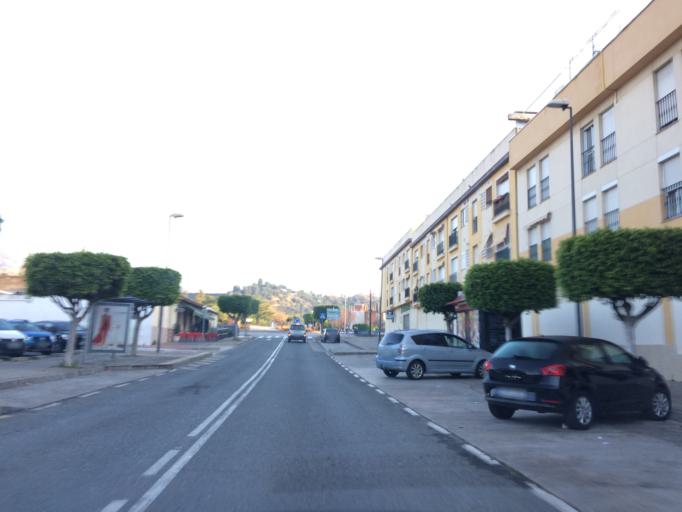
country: ES
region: Andalusia
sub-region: Provincia de Malaga
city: Malaga
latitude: 36.7528
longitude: -4.4240
